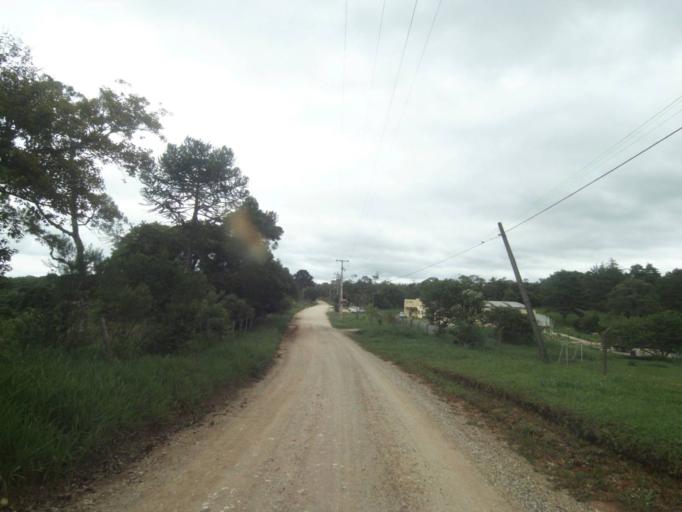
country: BR
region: Parana
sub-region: Quatro Barras
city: Quatro Barras
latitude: -25.3278
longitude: -49.0919
